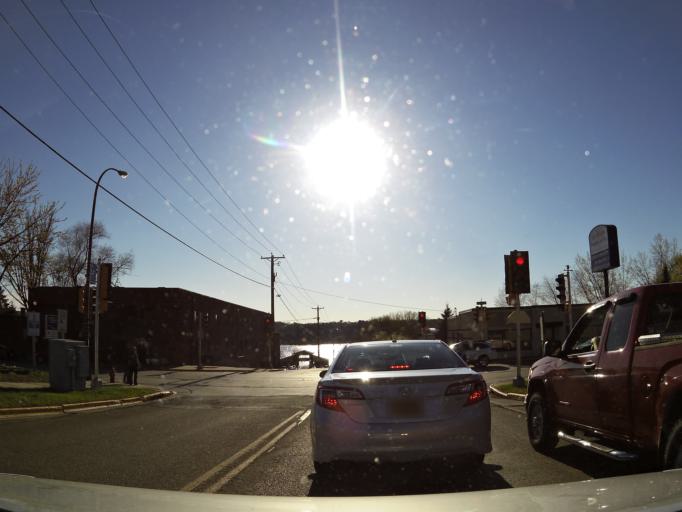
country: US
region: Wisconsin
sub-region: Saint Croix County
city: Hudson
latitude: 44.9770
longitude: -92.7567
